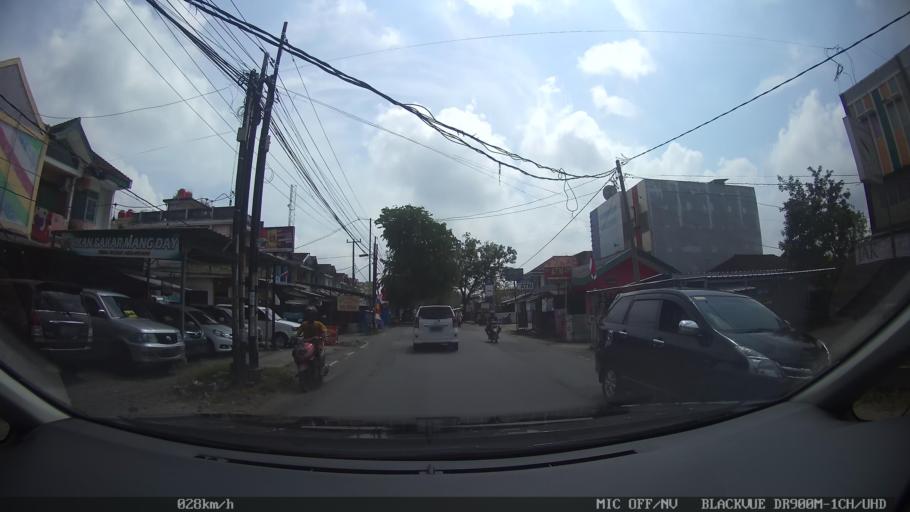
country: ID
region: Lampung
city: Kedaton
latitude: -5.3606
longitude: 105.2819
